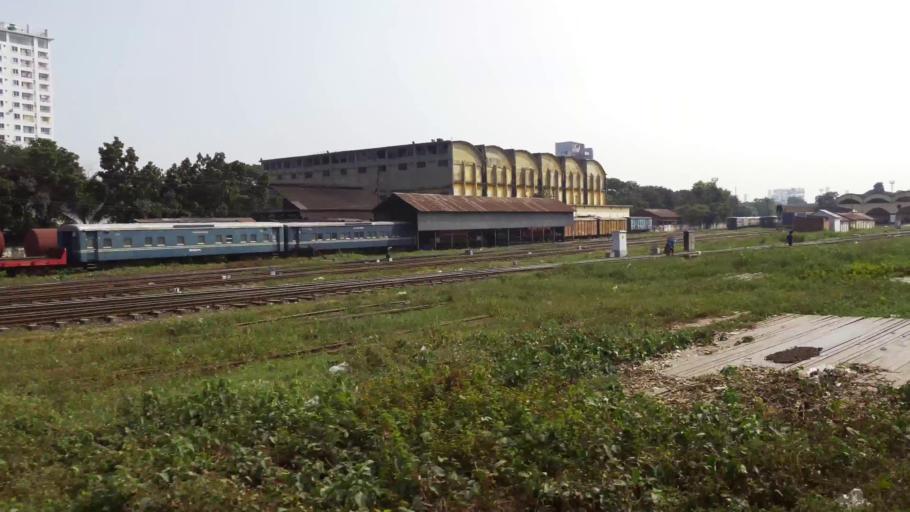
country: BD
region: Dhaka
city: Paltan
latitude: 23.7457
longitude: 90.4258
